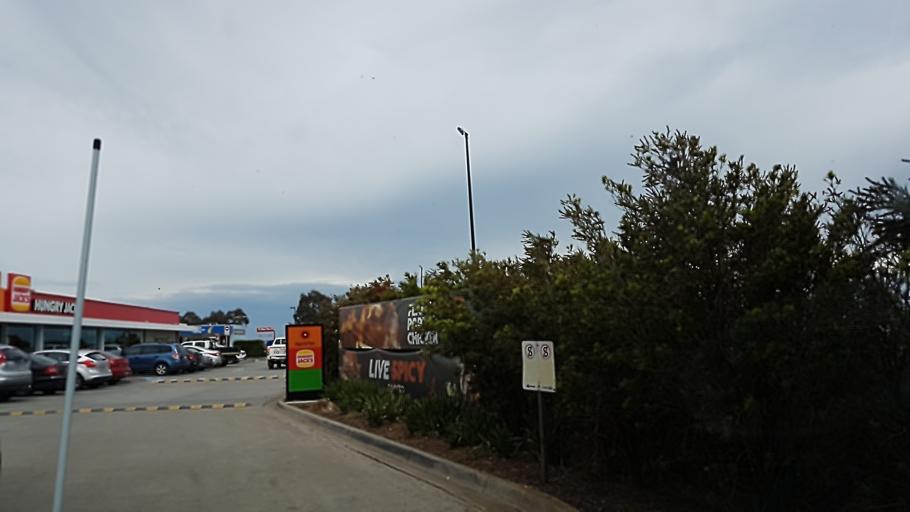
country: AU
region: Victoria
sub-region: Wyndham
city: Little River
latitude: -38.0024
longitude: 144.4925
